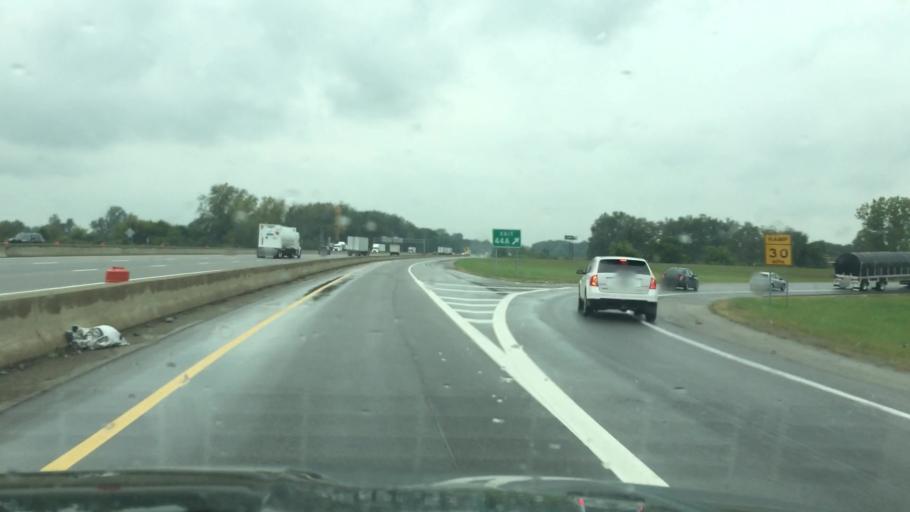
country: US
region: Ohio
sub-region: Clark County
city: Holiday Valley
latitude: 39.8655
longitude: -83.9946
